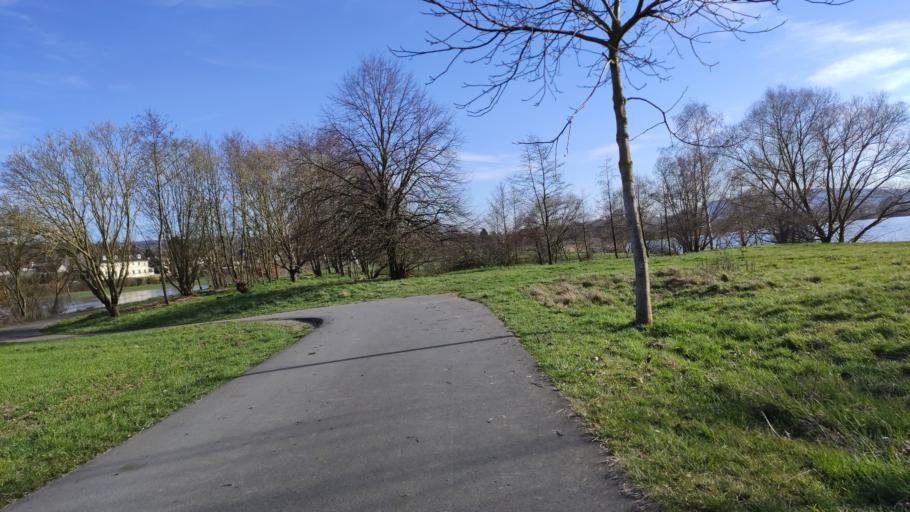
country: DE
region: Lower Saxony
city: Boffzen
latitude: 51.7548
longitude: 9.3838
